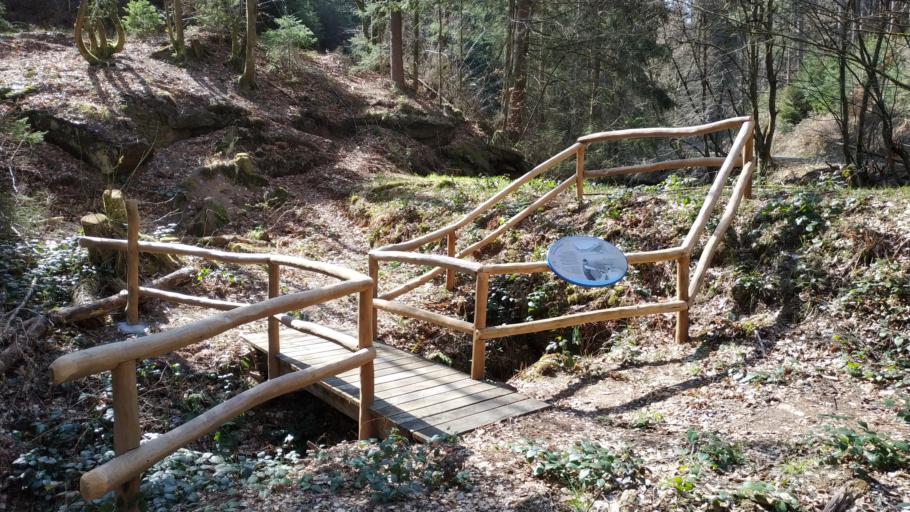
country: DE
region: Rheinland-Pfalz
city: Elmstein
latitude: 49.3816
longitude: 7.9167
